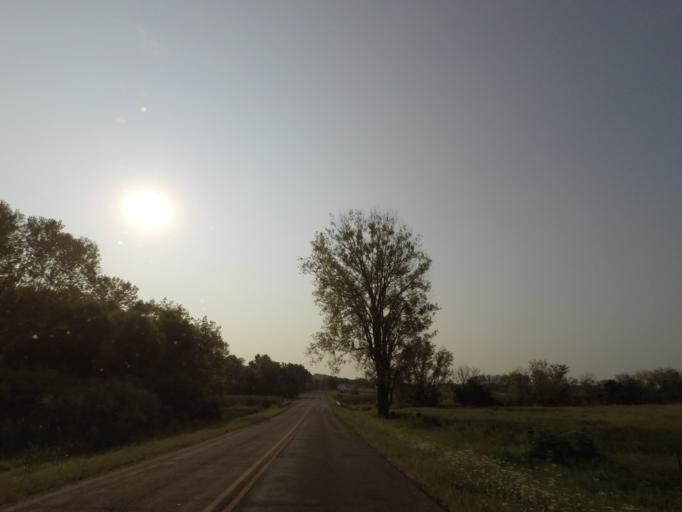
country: US
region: Wisconsin
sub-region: Dane County
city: Cottage Grove
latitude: 43.0450
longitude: -89.2345
